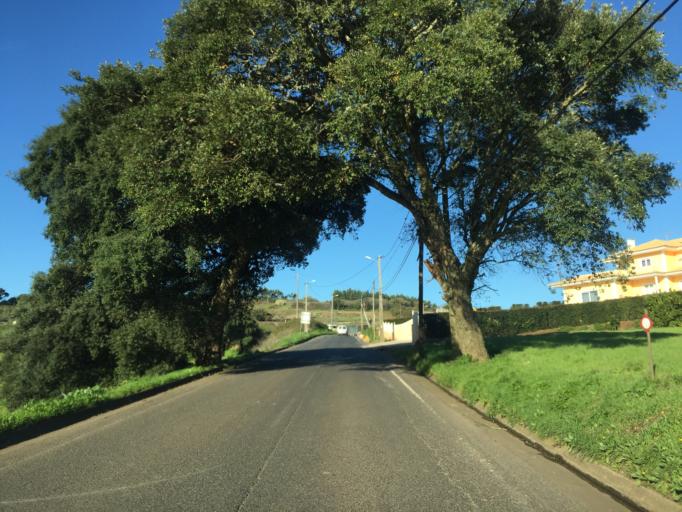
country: PT
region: Lisbon
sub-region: Sintra
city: Almargem
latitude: 38.8439
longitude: -9.2593
